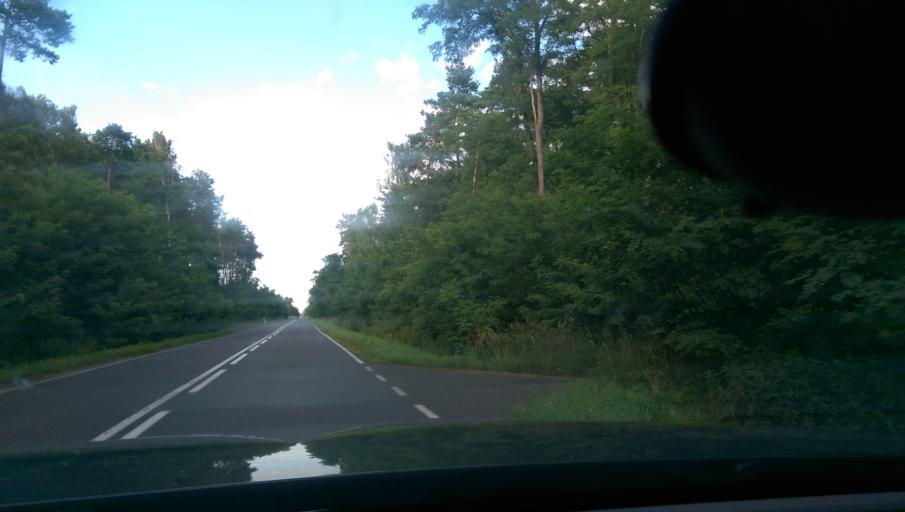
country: PL
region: Lubusz
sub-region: Powiat slubicki
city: Osno Lubuskie
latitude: 52.5086
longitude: 14.9108
